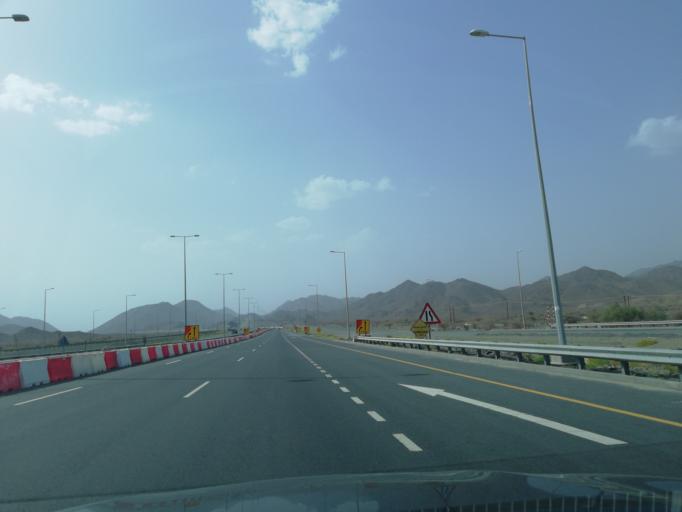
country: OM
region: Muhafazat ad Dakhiliyah
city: Sufalat Sama'il
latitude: 23.0857
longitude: 58.1818
